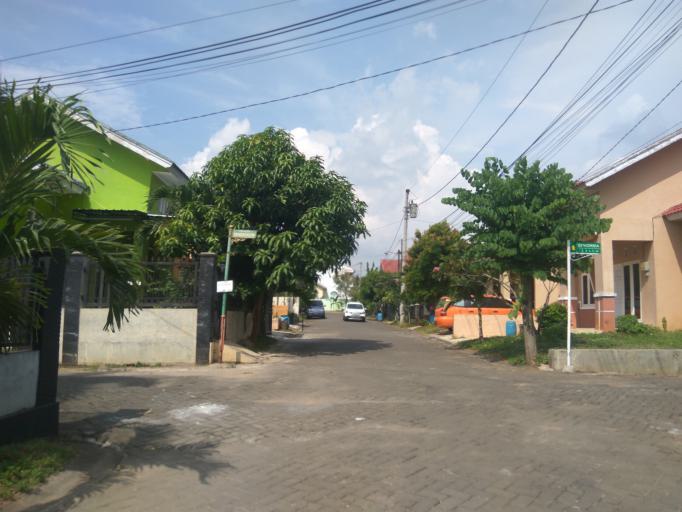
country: ID
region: Central Java
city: Ungaran
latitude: -7.0731
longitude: 110.4446
